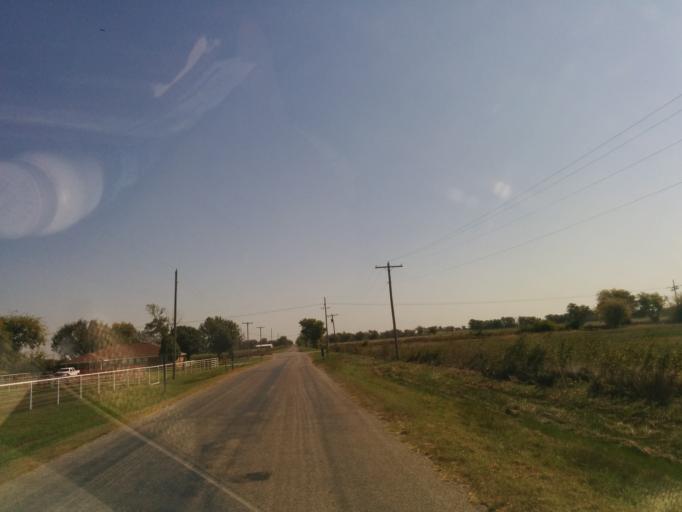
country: US
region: Oklahoma
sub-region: Okmulgee County
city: Beggs
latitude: 35.7991
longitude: -96.0706
